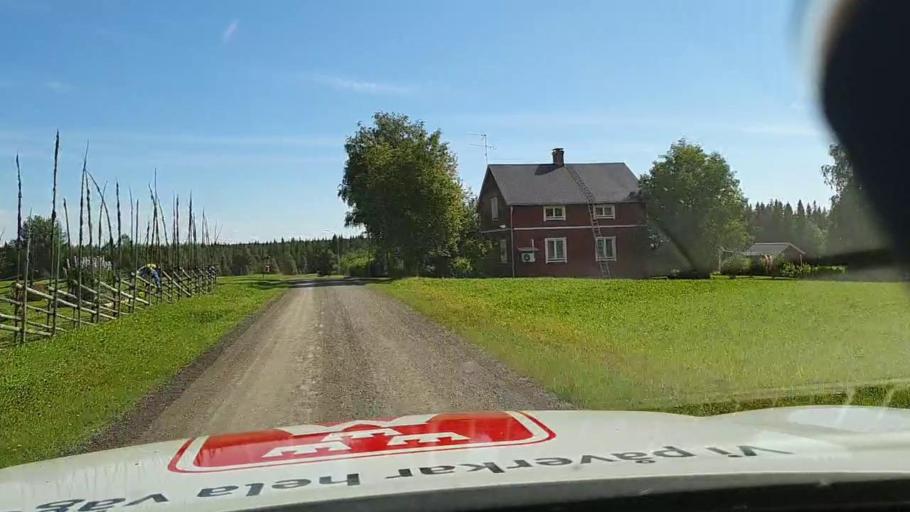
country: SE
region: Jaemtland
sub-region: Stroemsunds Kommun
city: Stroemsund
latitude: 63.7644
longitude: 15.3438
